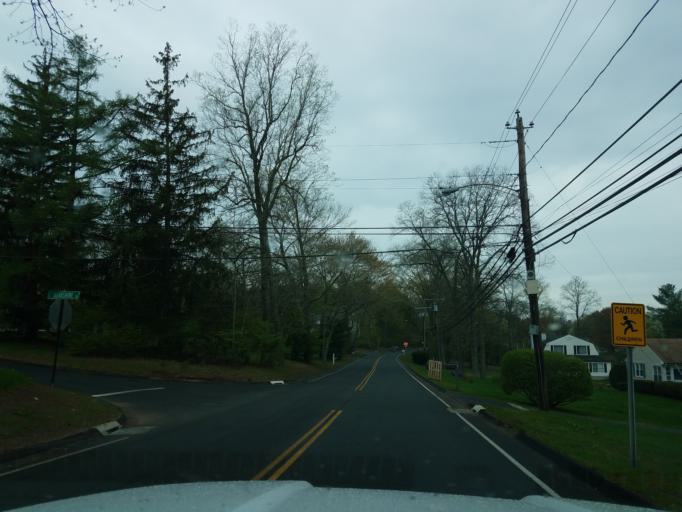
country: US
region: Connecticut
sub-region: Hartford County
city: Farmington
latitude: 41.7227
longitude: -72.7804
